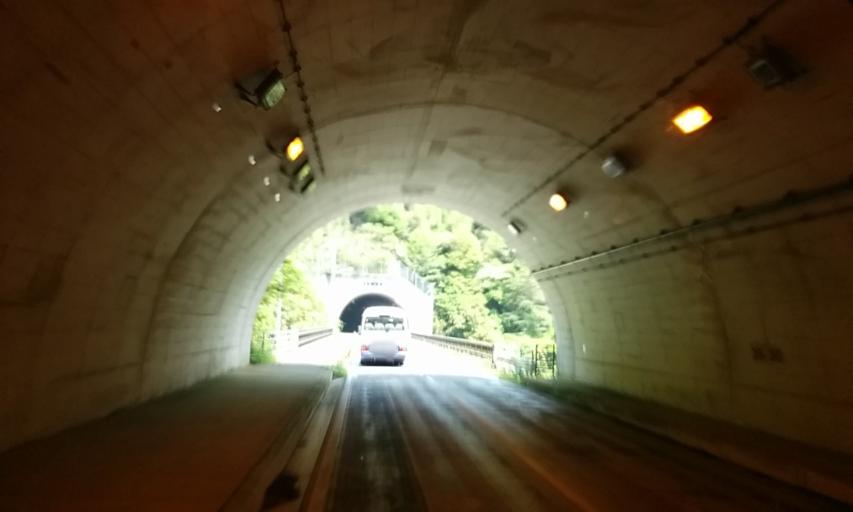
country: JP
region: Ehime
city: Niihama
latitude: 33.8875
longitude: 133.3062
